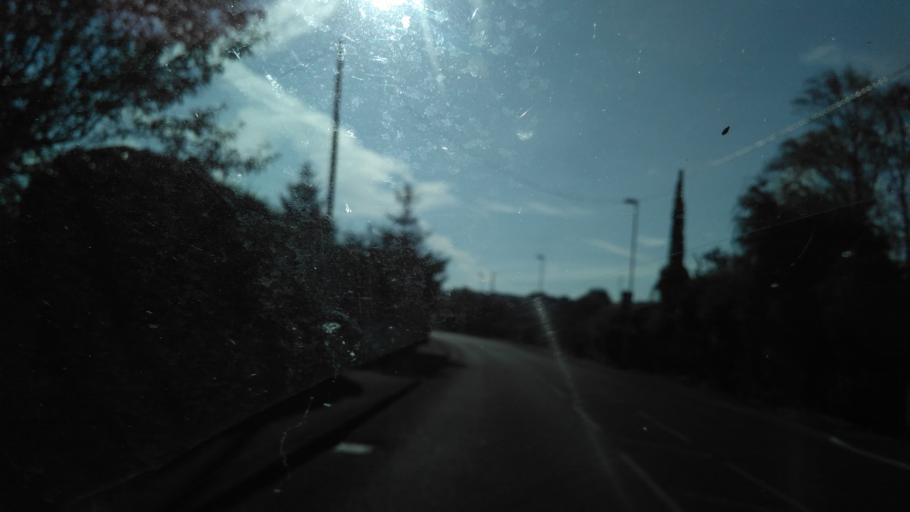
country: GB
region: England
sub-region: Kent
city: Whitstable
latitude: 51.3427
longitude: 0.9982
